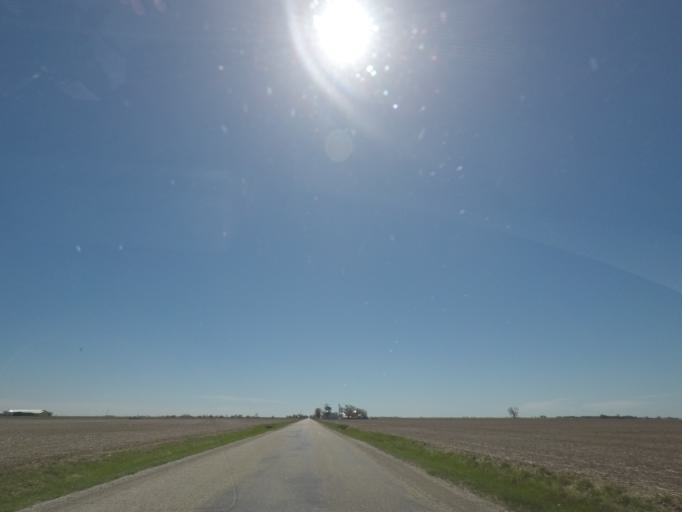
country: US
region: Illinois
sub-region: Logan County
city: Atlanta
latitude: 40.2051
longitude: -89.1943
